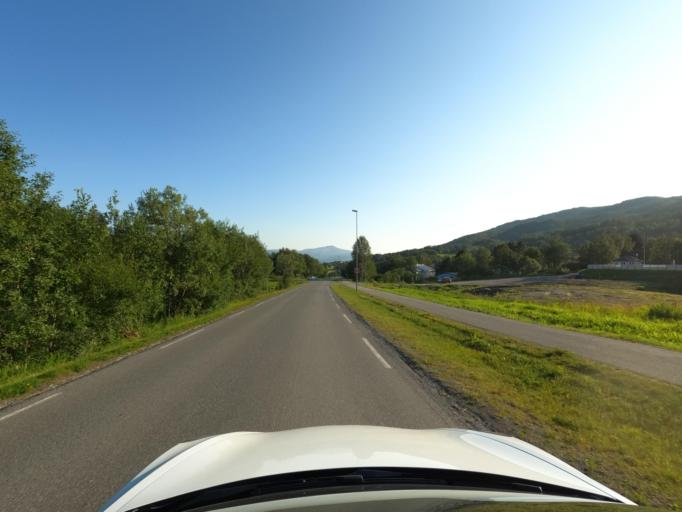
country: NO
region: Nordland
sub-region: Evenes
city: Randa
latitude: 68.4838
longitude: 16.8942
